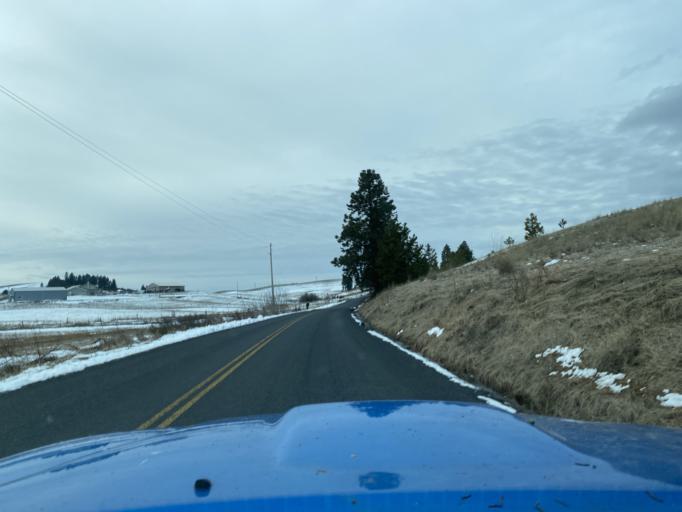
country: US
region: Idaho
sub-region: Latah County
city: Moscow
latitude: 46.6950
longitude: -116.9236
